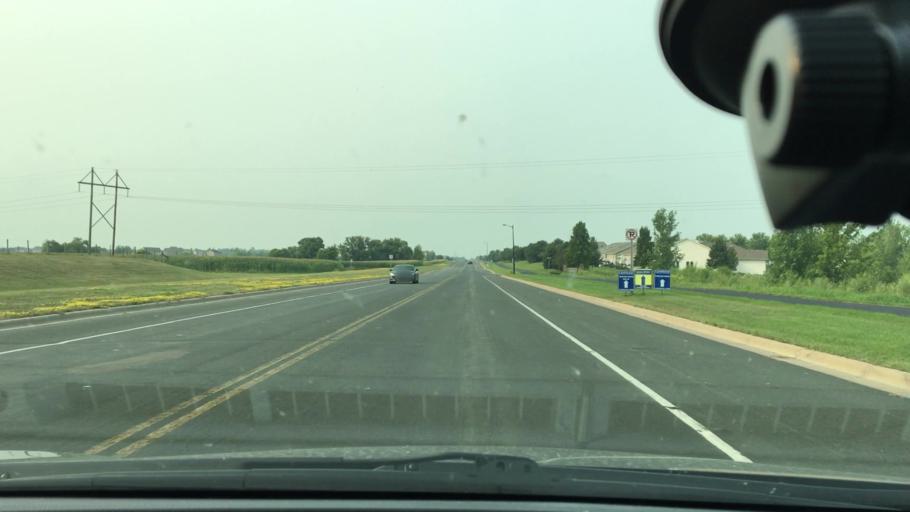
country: US
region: Minnesota
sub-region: Wright County
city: Albertville
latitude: 45.2419
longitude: -93.6427
